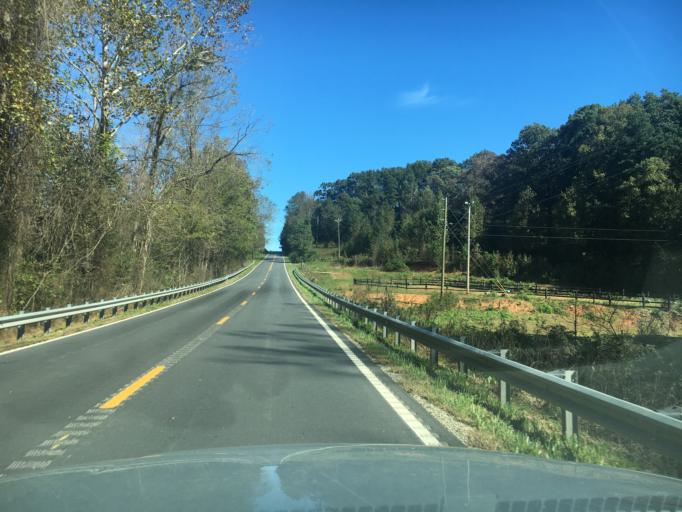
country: US
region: North Carolina
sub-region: Burke County
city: Glen Alpine
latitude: 35.6053
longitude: -81.8168
